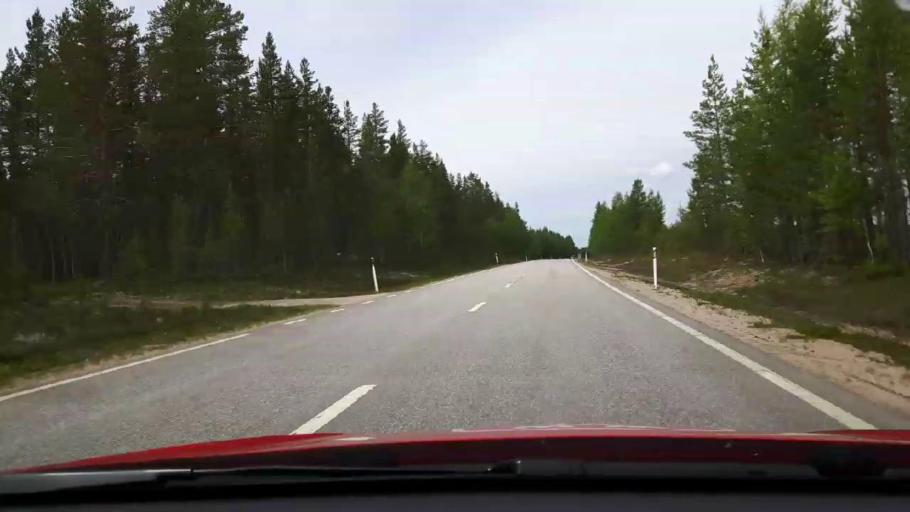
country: SE
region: Jaemtland
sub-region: Harjedalens Kommun
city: Sveg
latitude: 62.1125
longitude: 14.1828
